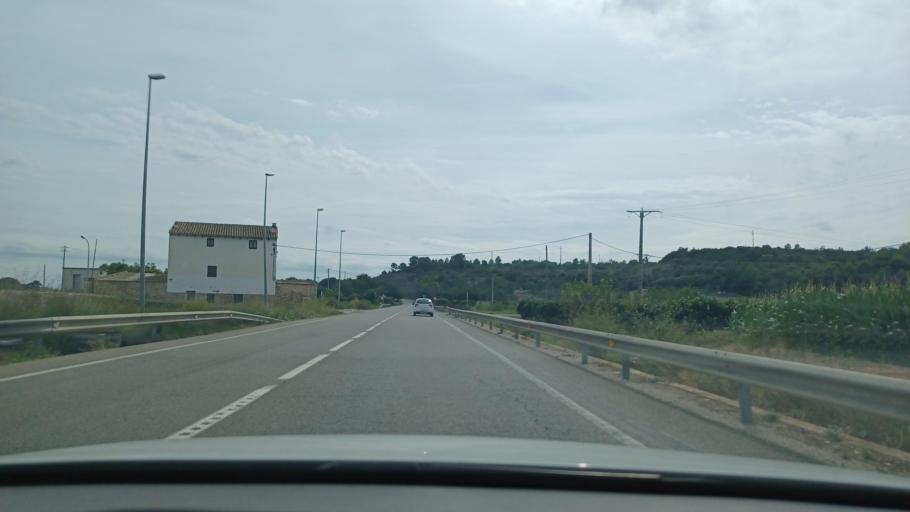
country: ES
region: Catalonia
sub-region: Provincia de Tarragona
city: Tortosa
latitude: 40.7788
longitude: 0.5065
